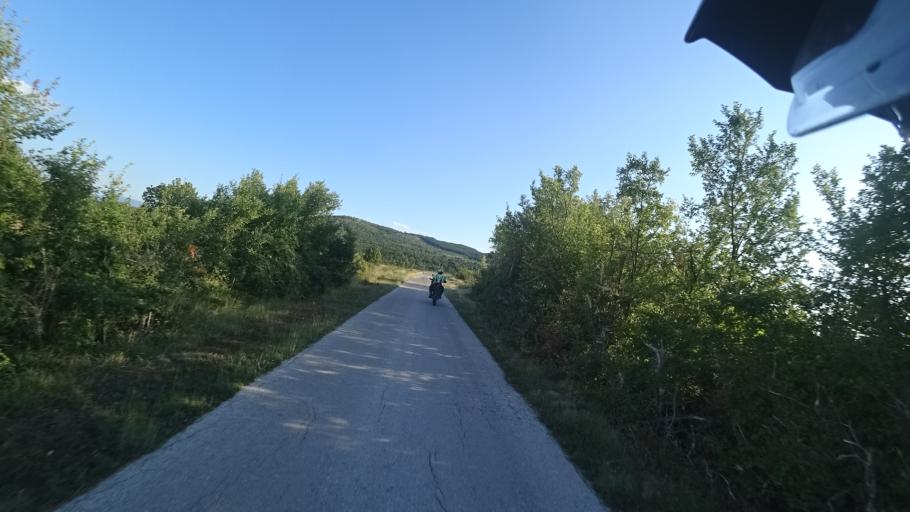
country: HR
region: Sibensko-Kniniska
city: Knin
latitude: 44.1220
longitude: 16.1372
